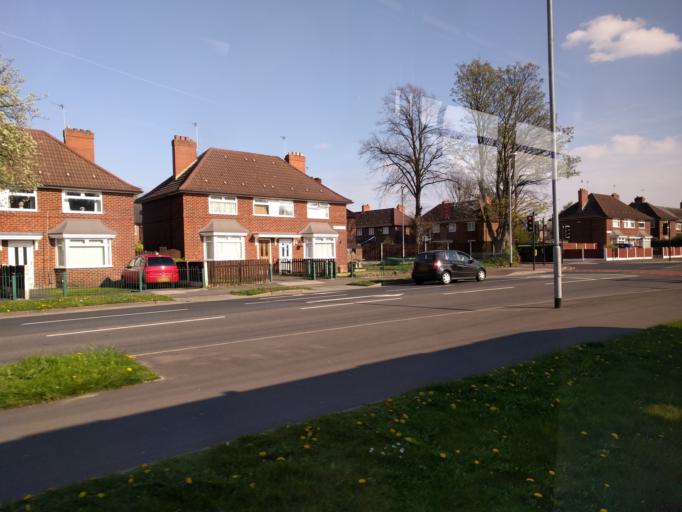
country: GB
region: England
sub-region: Manchester
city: Didsbury
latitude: 53.3860
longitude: -2.2560
